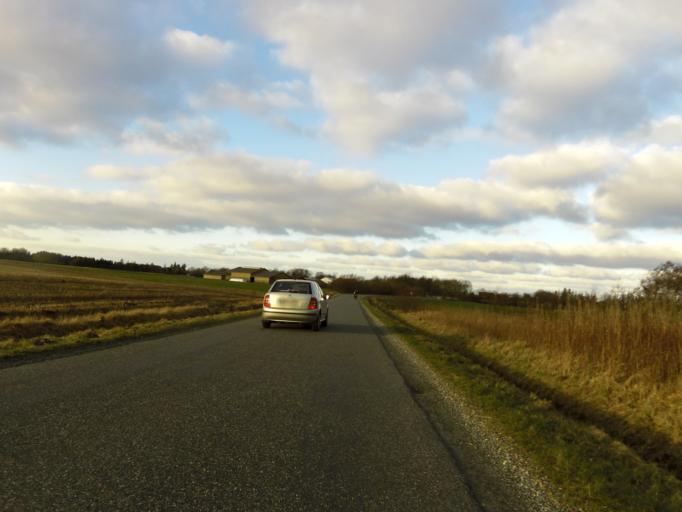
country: DK
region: South Denmark
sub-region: Esbjerg Kommune
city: Ribe
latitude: 55.3024
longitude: 8.8488
